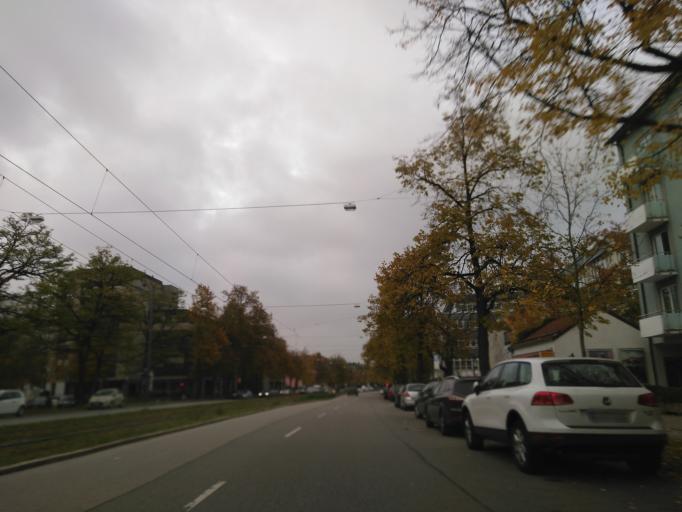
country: DE
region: Bavaria
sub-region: Upper Bavaria
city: Munich
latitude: 48.1125
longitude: 11.5932
